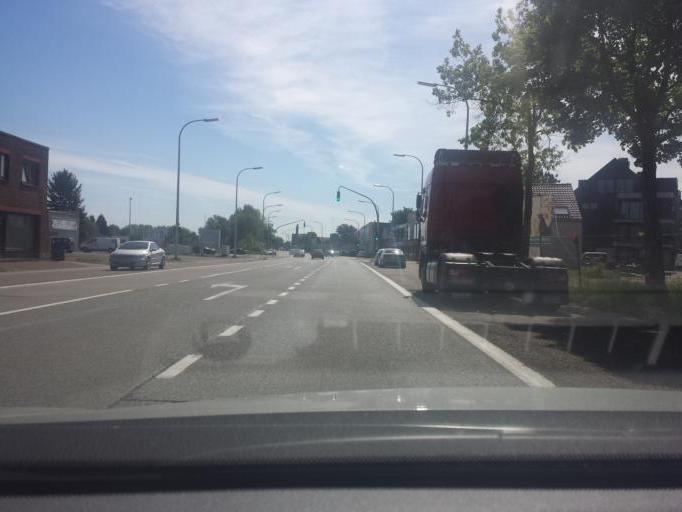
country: BE
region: Flanders
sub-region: Provincie Limburg
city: Halen
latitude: 50.9498
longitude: 5.1142
